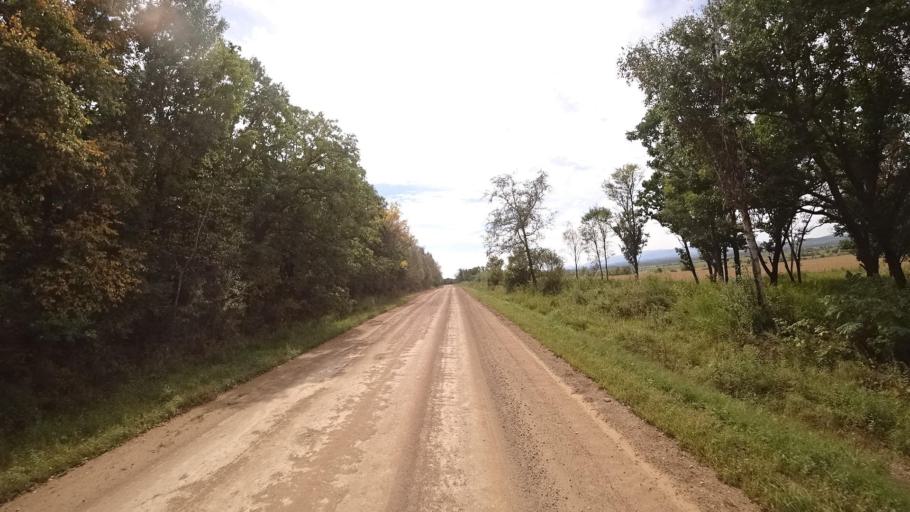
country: RU
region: Primorskiy
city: Yakovlevka
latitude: 44.5770
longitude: 133.5956
